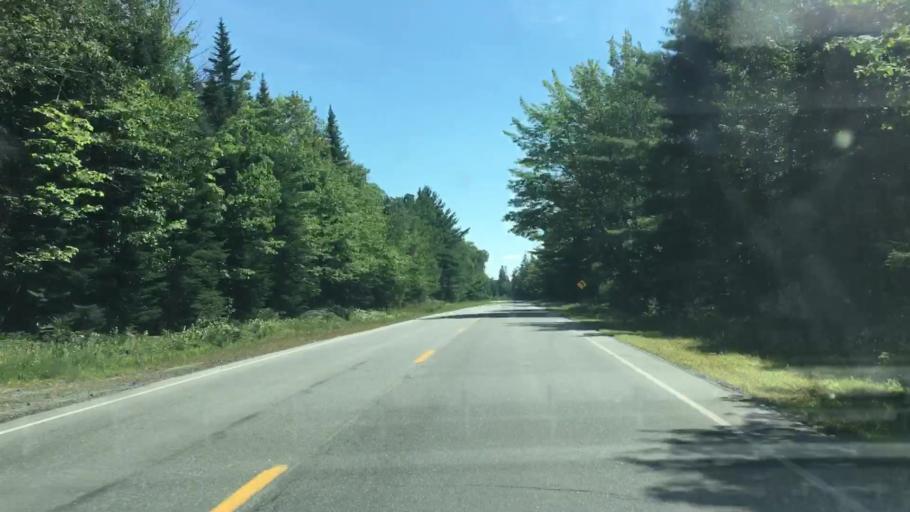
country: US
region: Maine
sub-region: Piscataquis County
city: Milo
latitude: 45.2035
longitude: -68.9078
